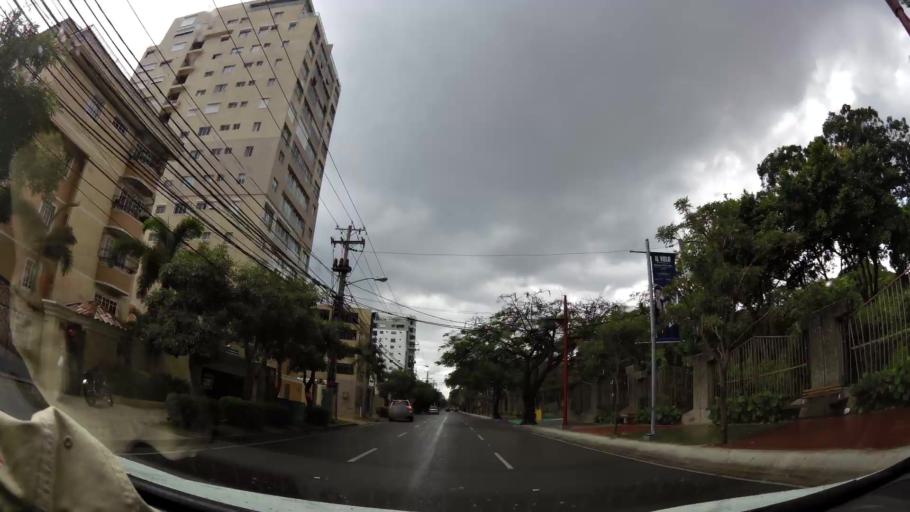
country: DO
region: Nacional
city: La Julia
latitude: 18.4652
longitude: -69.9186
